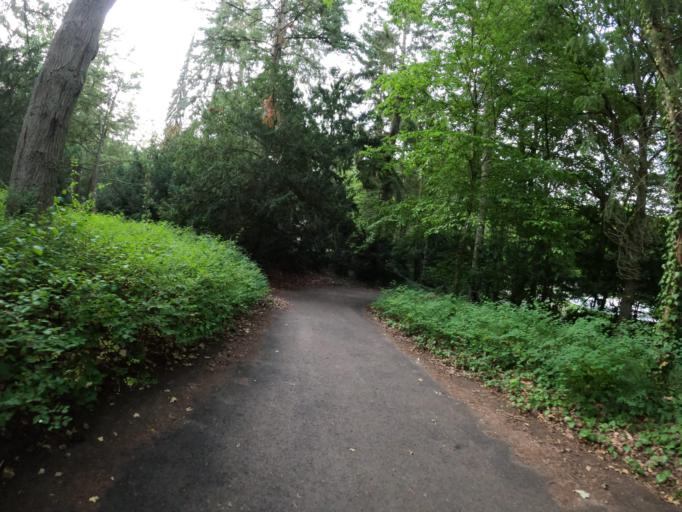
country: PL
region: West Pomeranian Voivodeship
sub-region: Szczecin
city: Szczecin
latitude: 53.4184
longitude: 14.5250
